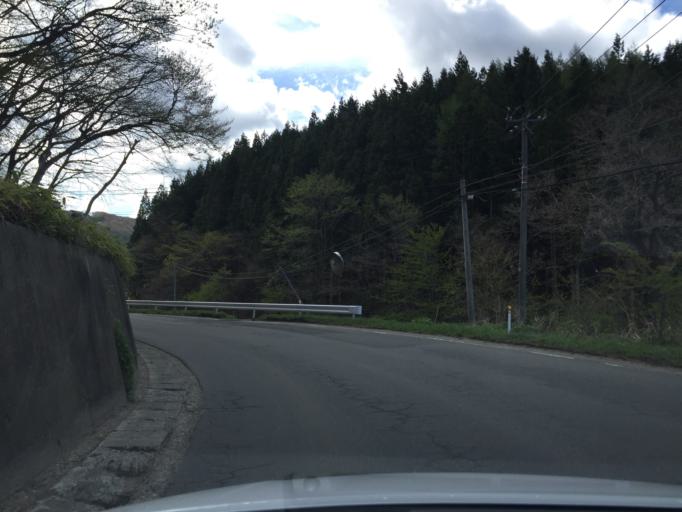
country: JP
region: Fukushima
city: Funehikimachi-funehiki
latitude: 37.5881
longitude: 140.6895
